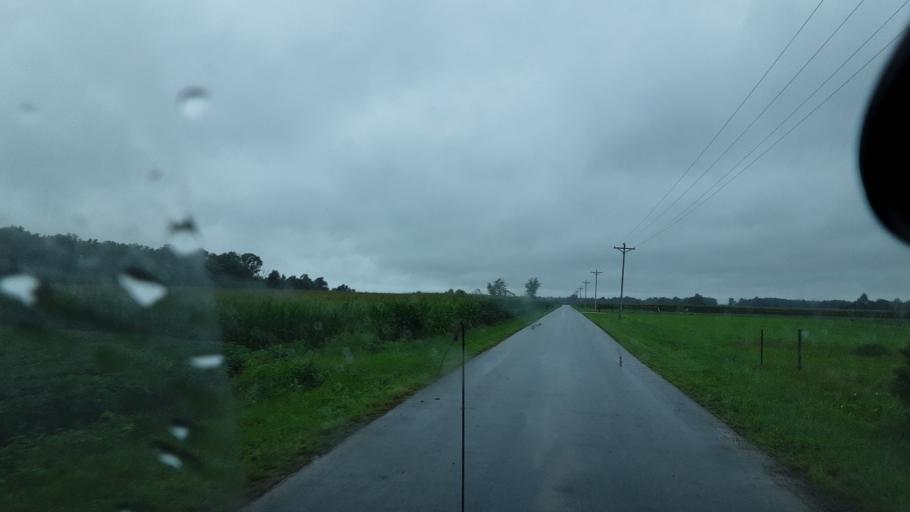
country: US
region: Indiana
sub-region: Adams County
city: Decatur
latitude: 40.7533
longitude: -84.8568
